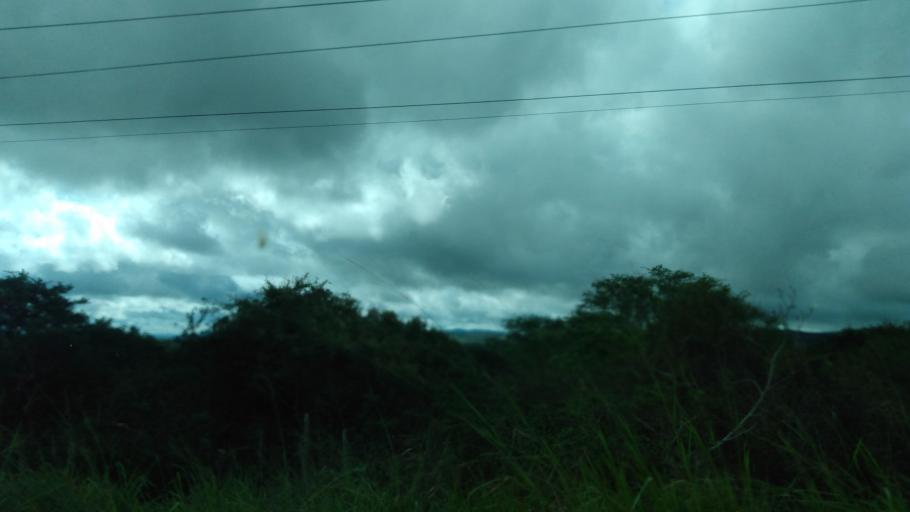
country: BR
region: Pernambuco
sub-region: Caruaru
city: Caruaru
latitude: -8.3245
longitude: -35.9818
